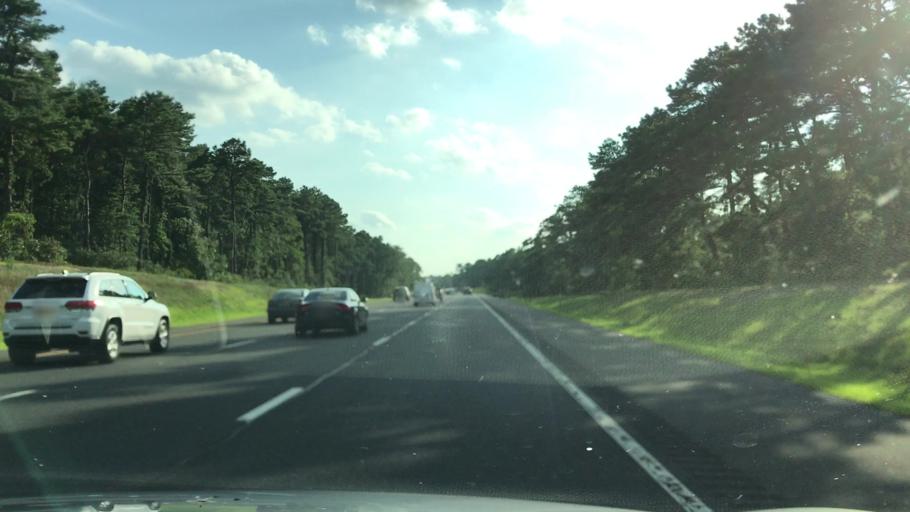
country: US
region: New Jersey
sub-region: Ocean County
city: Tuckerton
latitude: 39.6365
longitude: -74.3755
